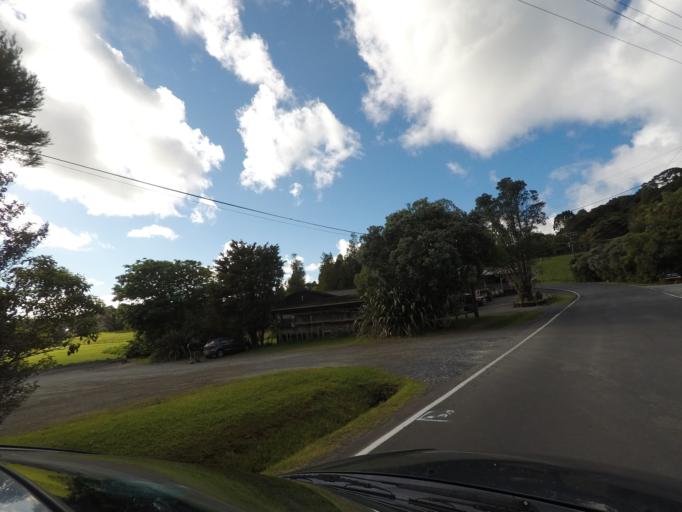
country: NZ
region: Auckland
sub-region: Auckland
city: Titirangi
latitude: -37.0045
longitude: 174.5621
